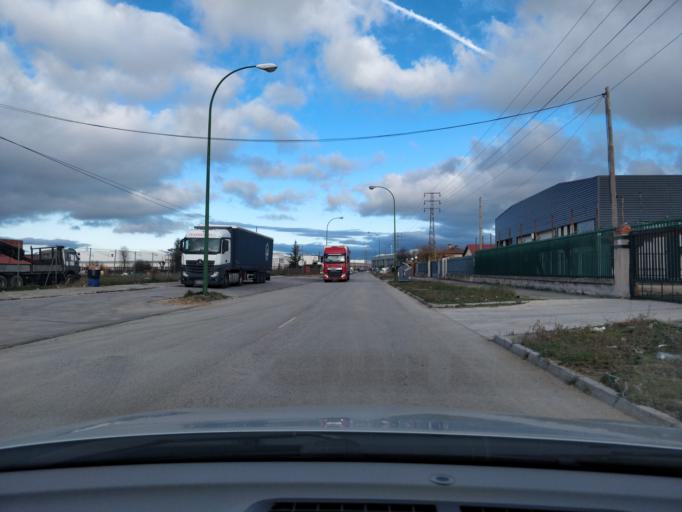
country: ES
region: Castille and Leon
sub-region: Provincia de Burgos
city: Villalbilla de Burgos
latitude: 42.3589
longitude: -3.7605
